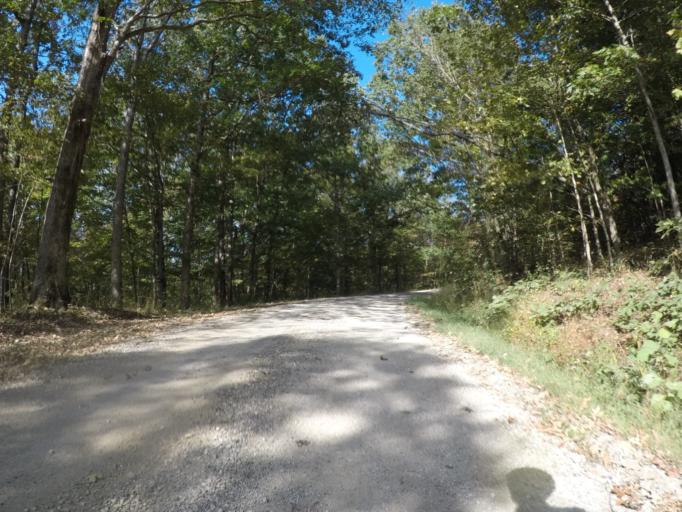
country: US
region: West Virginia
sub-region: Cabell County
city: Lesage
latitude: 38.6370
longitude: -82.4017
